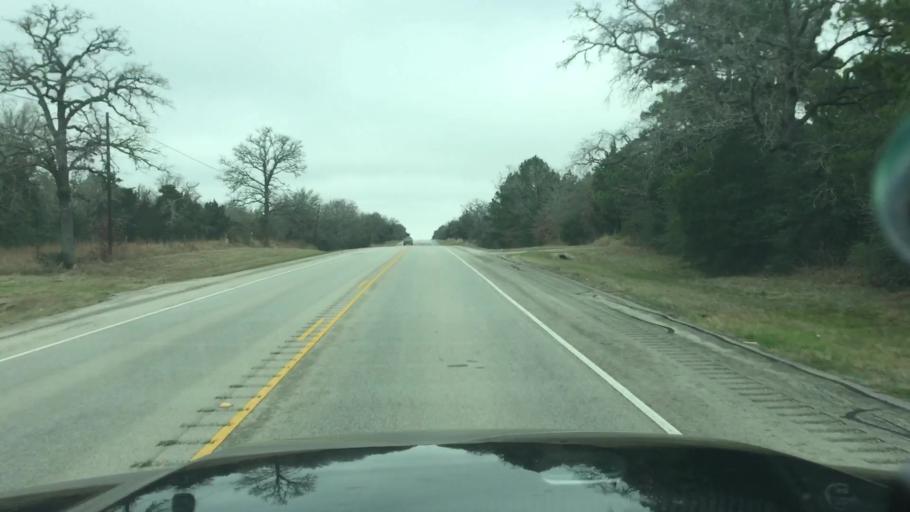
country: US
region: Texas
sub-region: Lee County
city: Giddings
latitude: 30.0727
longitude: -96.9168
